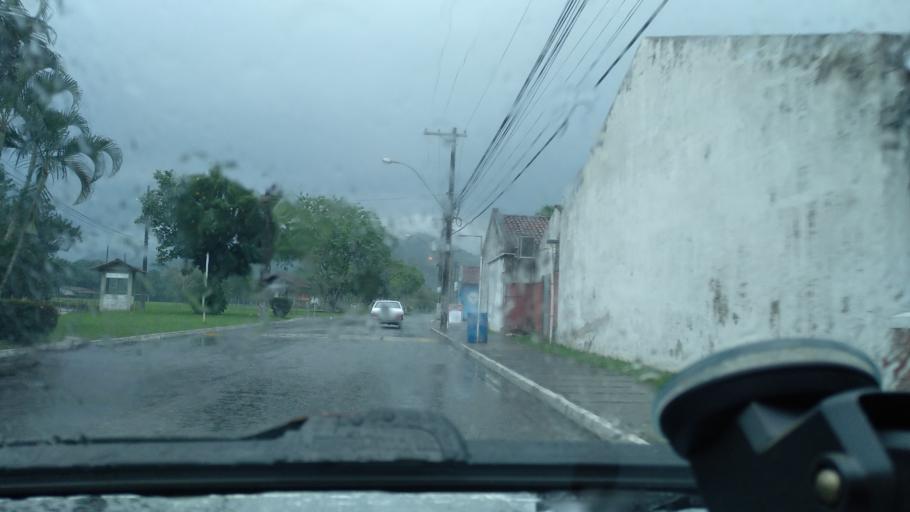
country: BR
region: Rio de Janeiro
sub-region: Angra Dos Reis
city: Angra dos Reis
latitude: -23.0281
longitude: -44.5391
